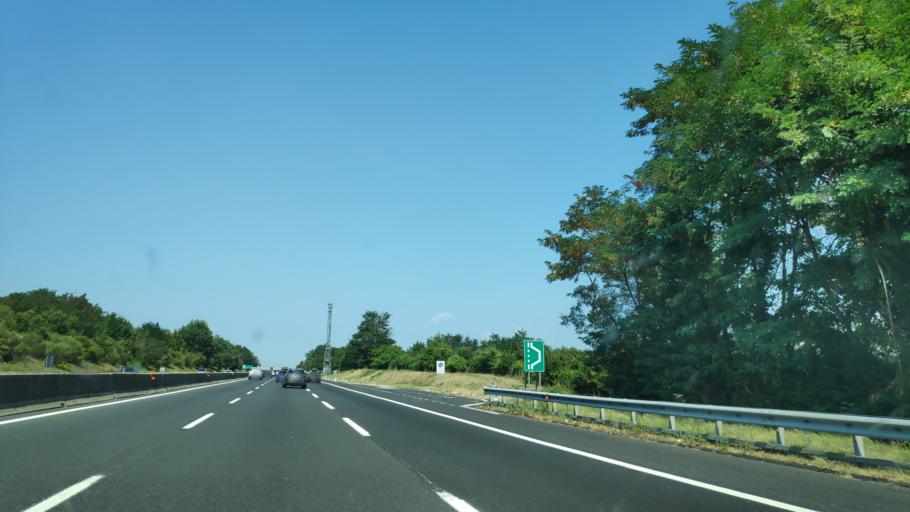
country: IT
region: Campania
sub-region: Provincia di Caserta
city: Mignano Monte Lungo
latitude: 41.4070
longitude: 13.9641
